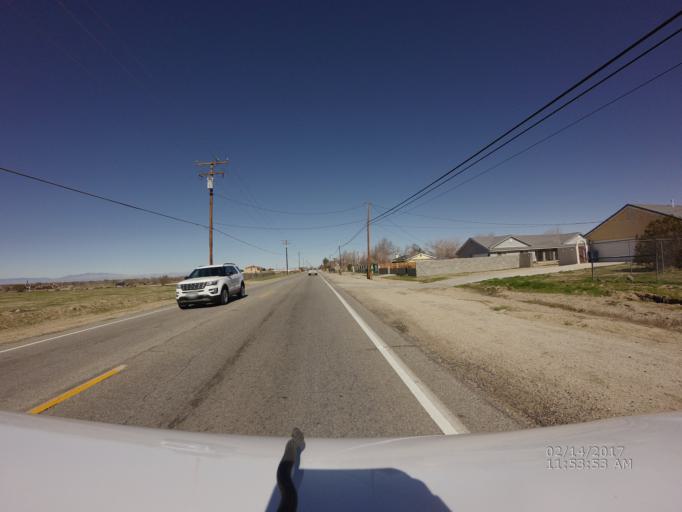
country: US
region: California
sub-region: Los Angeles County
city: Littlerock
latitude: 34.5619
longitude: -117.9696
